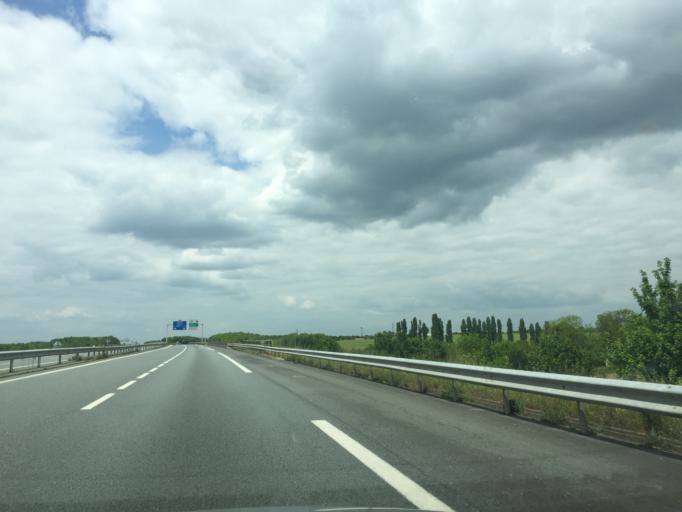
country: FR
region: Poitou-Charentes
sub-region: Departement des Deux-Sevres
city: Saint-Gelais
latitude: 46.4111
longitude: -0.3917
